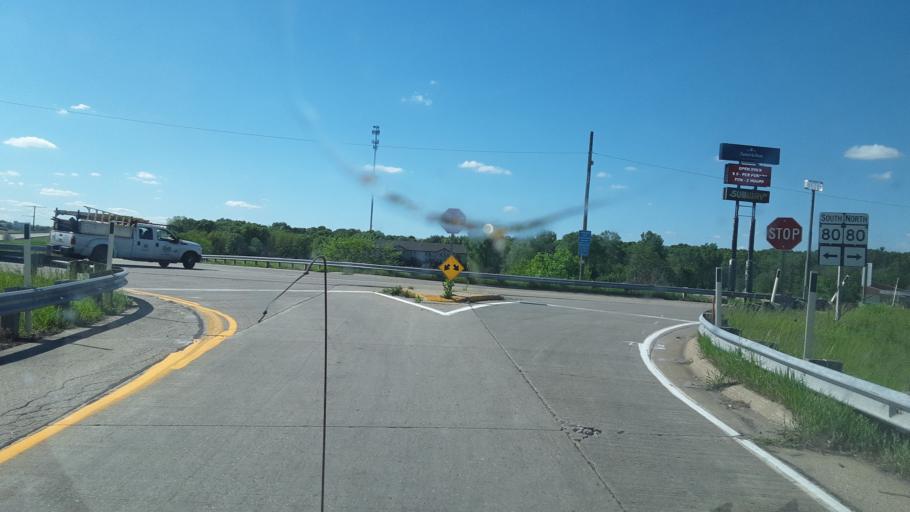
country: US
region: Wisconsin
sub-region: Juneau County
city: New Lisbon
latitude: 43.8833
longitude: -90.1463
